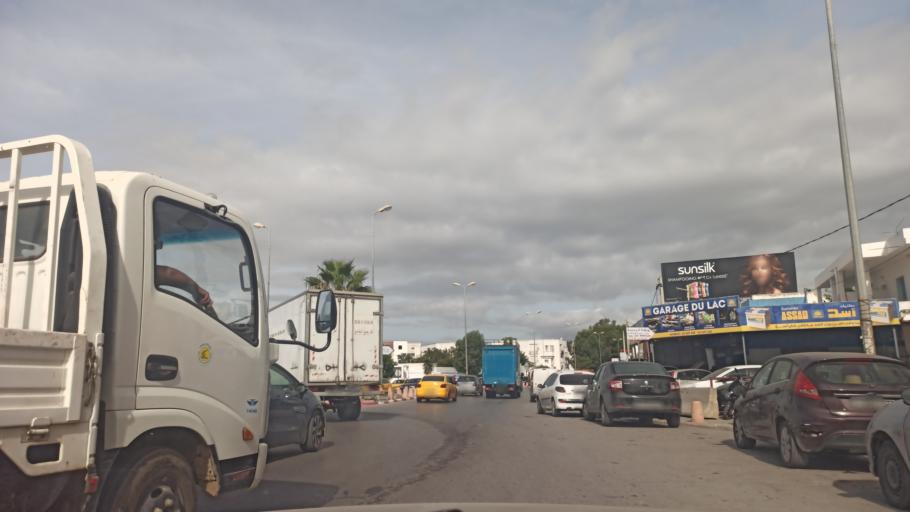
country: TN
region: Tunis
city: La Goulette
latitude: 36.8493
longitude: 10.2598
